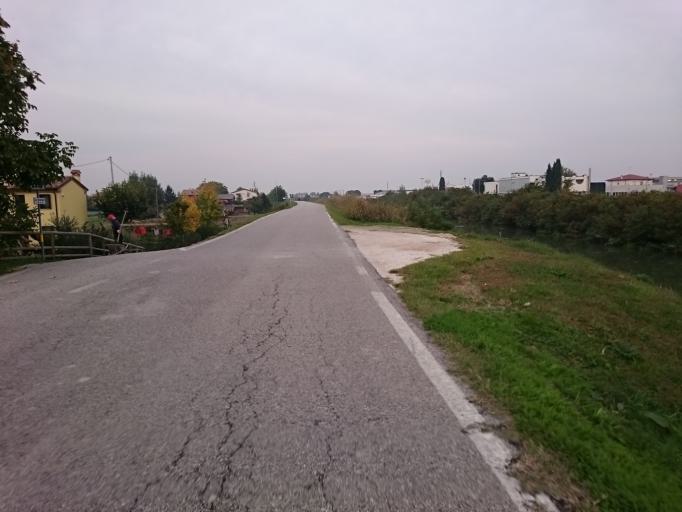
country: IT
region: Veneto
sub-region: Provincia di Padova
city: Terradura
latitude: 45.3291
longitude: 11.8157
